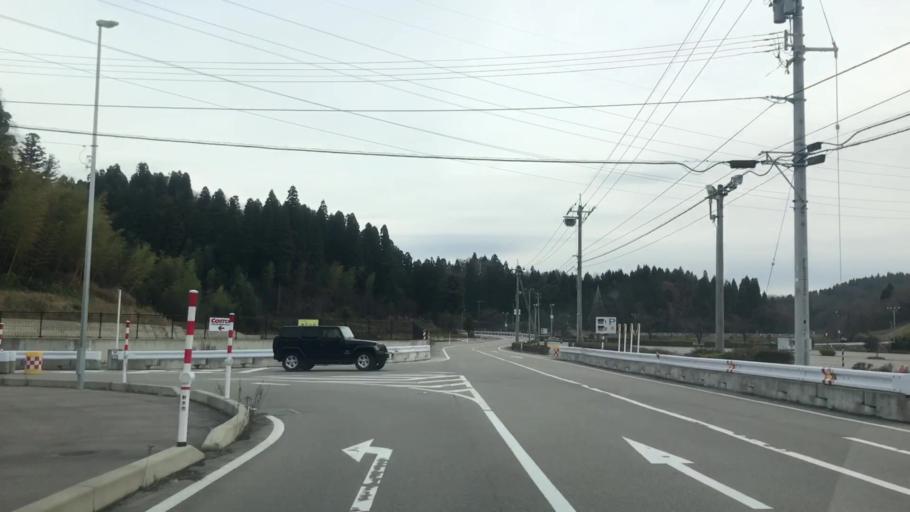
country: JP
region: Toyama
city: Kuragaki-kosugi
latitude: 36.6891
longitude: 137.0843
